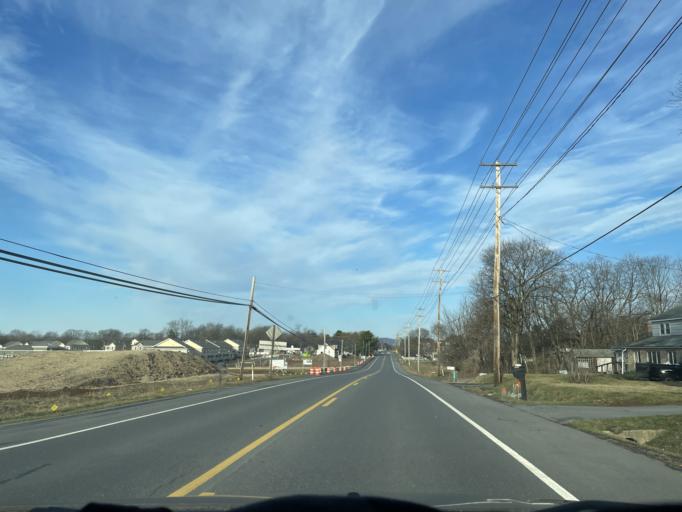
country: US
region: Maryland
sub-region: Washington County
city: Halfway
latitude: 39.6494
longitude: -77.7609
